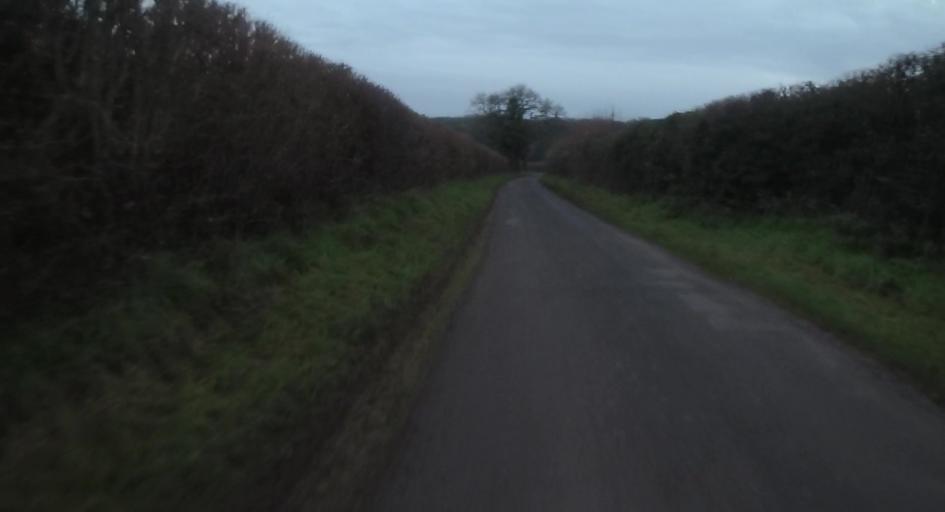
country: GB
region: England
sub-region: Hampshire
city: Overton
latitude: 51.2519
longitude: -1.3060
